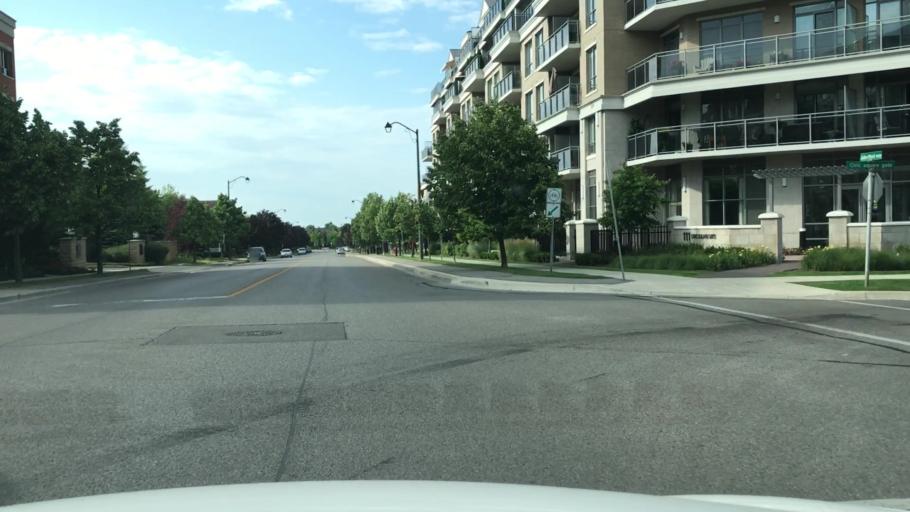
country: CA
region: Ontario
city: Newmarket
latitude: 44.0082
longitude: -79.4499
